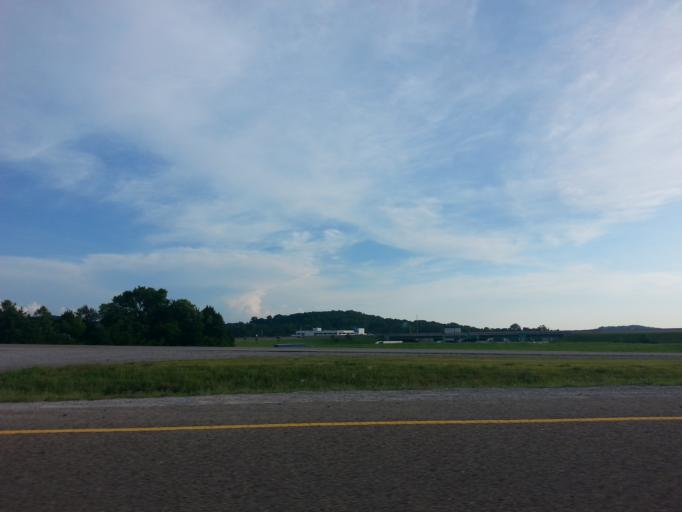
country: US
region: Tennessee
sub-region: Knox County
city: Farragut
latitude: 35.9135
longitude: -84.1190
